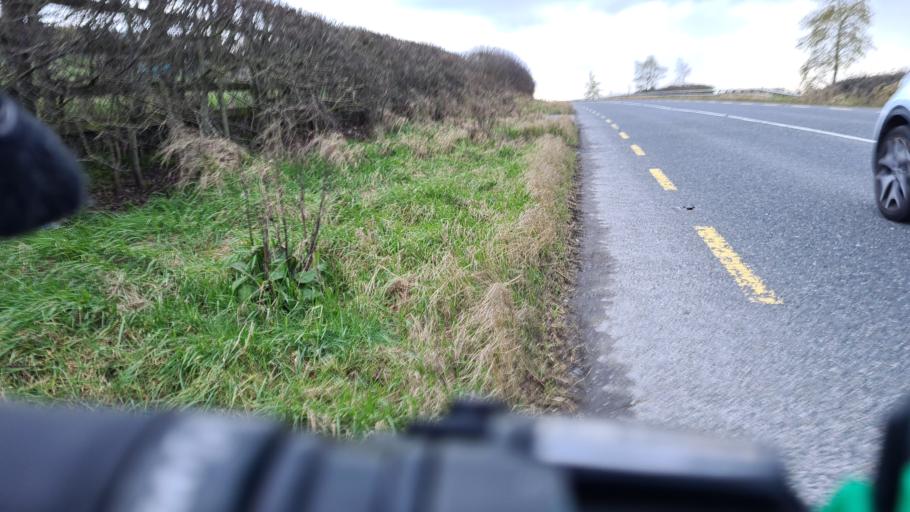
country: IE
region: Leinster
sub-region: Kildare
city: Maynooth
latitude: 53.3469
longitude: -6.6010
